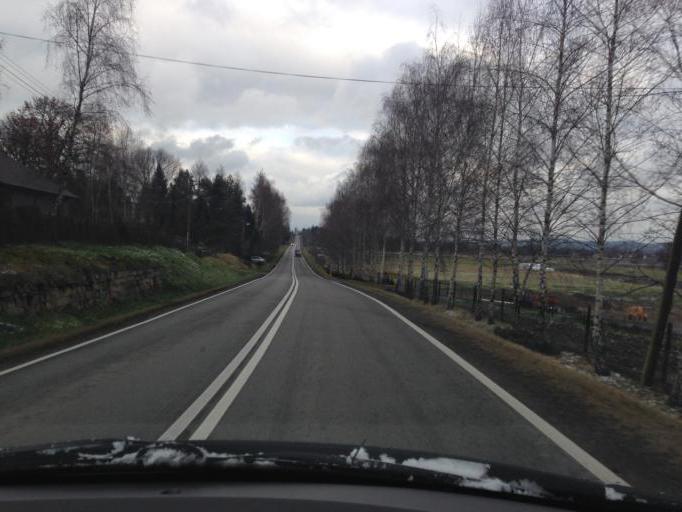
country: PL
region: Lesser Poland Voivodeship
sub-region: Powiat wielicki
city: Gdow
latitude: 49.9035
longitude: 20.1512
